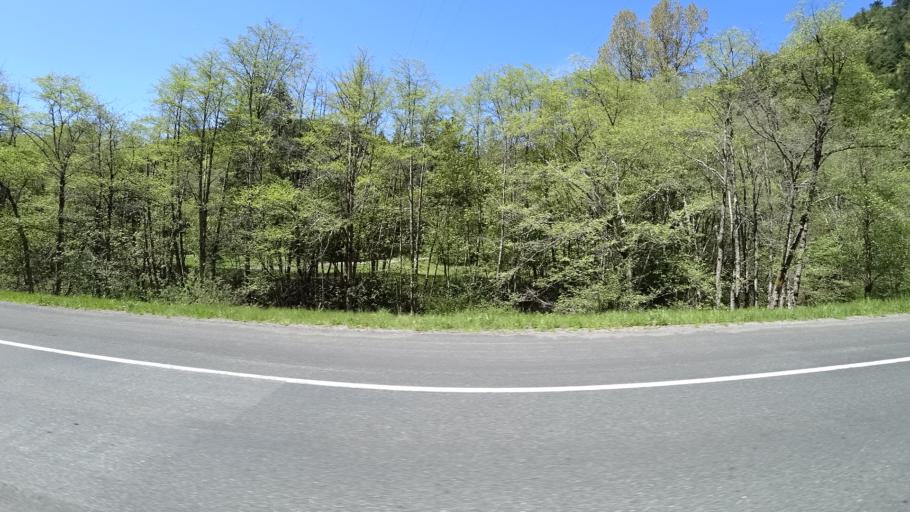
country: US
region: California
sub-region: Humboldt County
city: Willow Creek
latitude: 40.9199
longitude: -123.6976
